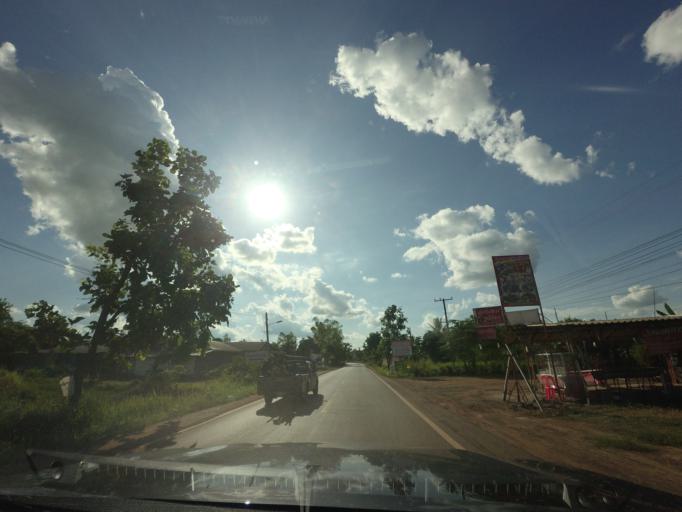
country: TH
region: Changwat Udon Thani
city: Ban Dung
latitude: 17.7449
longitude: 103.3197
